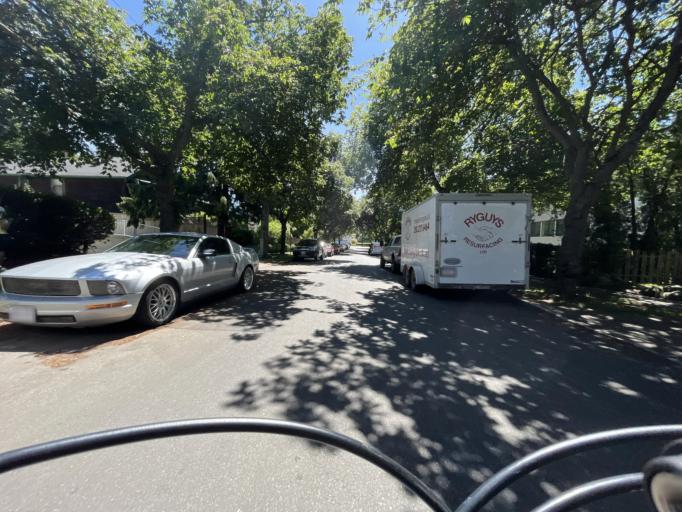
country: CA
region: British Columbia
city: Victoria
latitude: 48.4388
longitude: -123.3563
